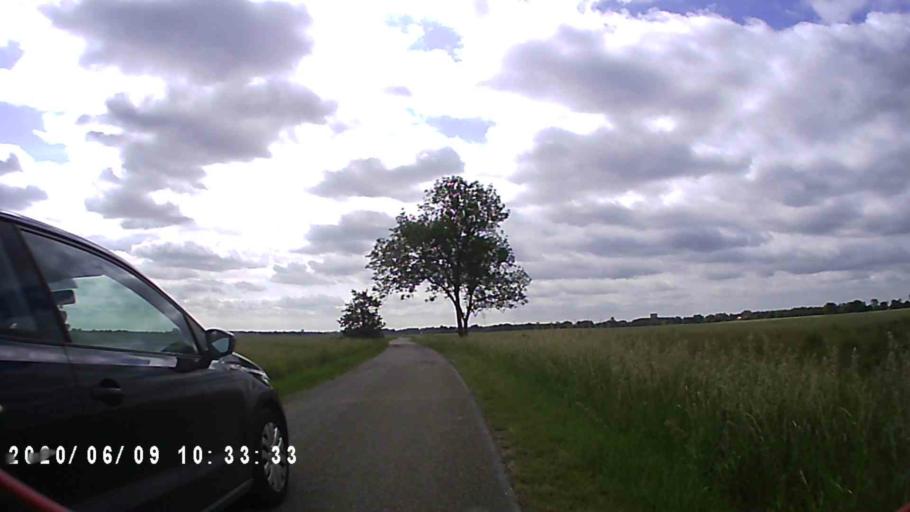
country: NL
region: Groningen
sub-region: Gemeente Zuidhorn
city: Aduard
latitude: 53.2669
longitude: 6.5143
